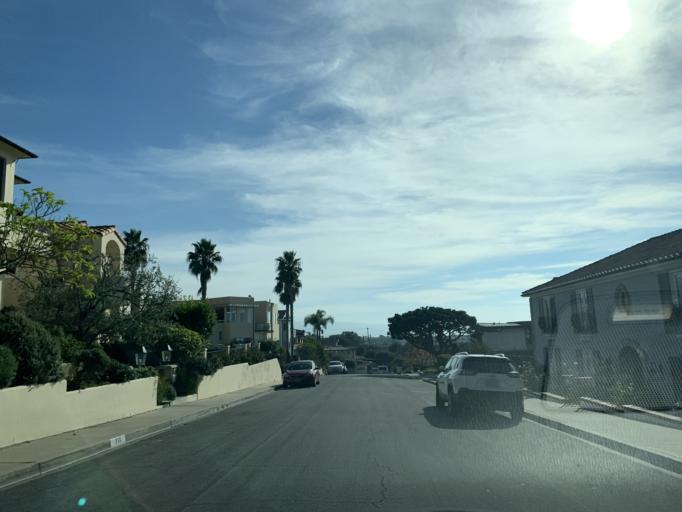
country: US
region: California
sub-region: Los Angeles County
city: Manhattan Beach
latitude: 33.8816
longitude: -118.4021
